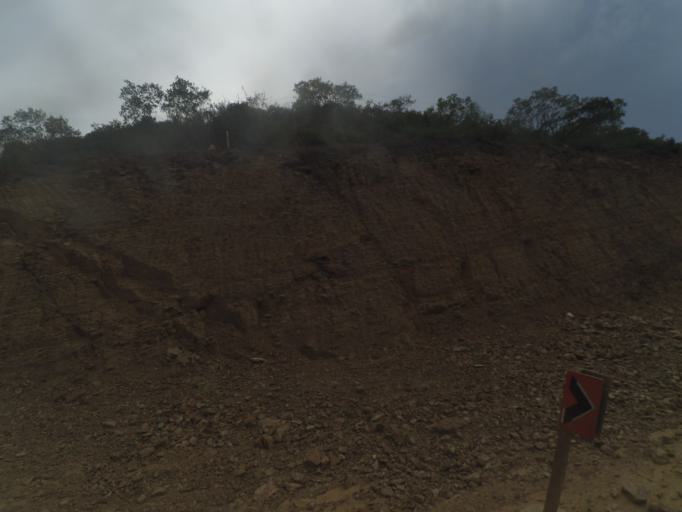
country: BO
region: Chuquisaca
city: Padilla
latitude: -19.3476
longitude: -64.2845
